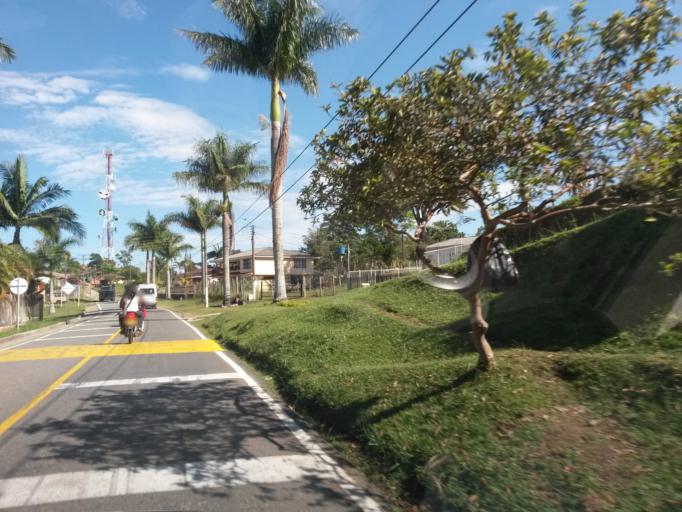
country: CO
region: Cauca
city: Morales
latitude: 2.7490
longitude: -76.6248
